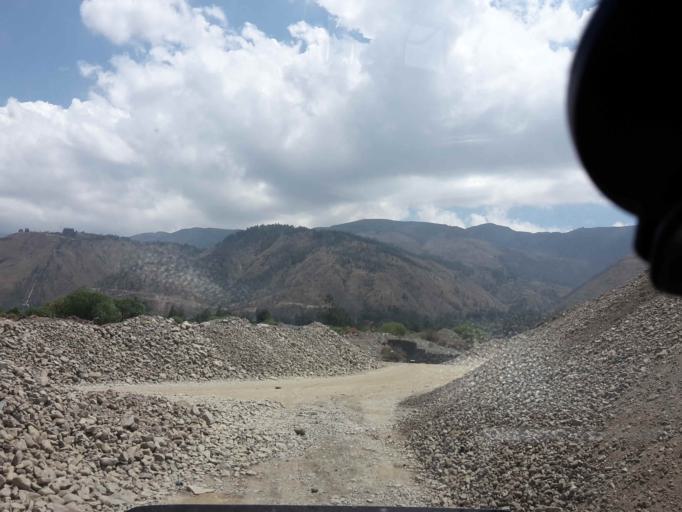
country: BO
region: Cochabamba
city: Cochabamba
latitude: -17.3323
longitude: -66.2116
